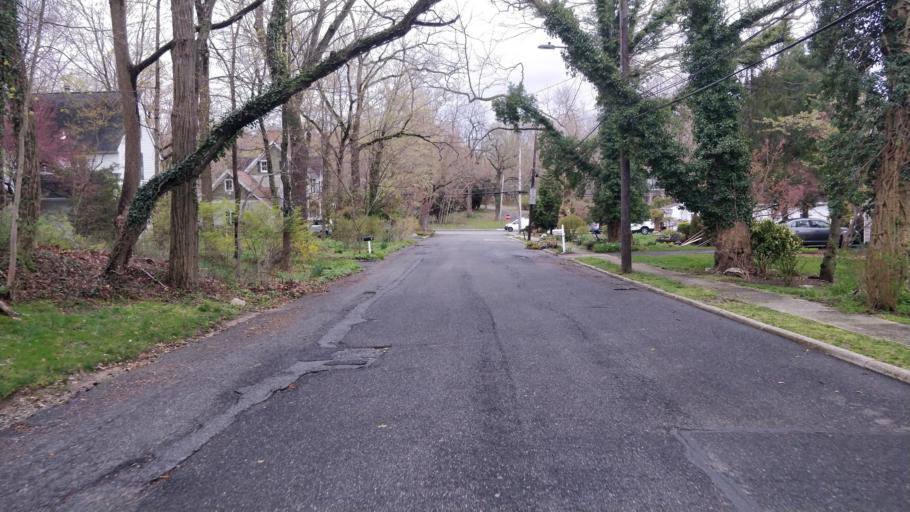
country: US
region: New York
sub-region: Suffolk County
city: East Setauket
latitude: 40.9447
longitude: -73.0983
